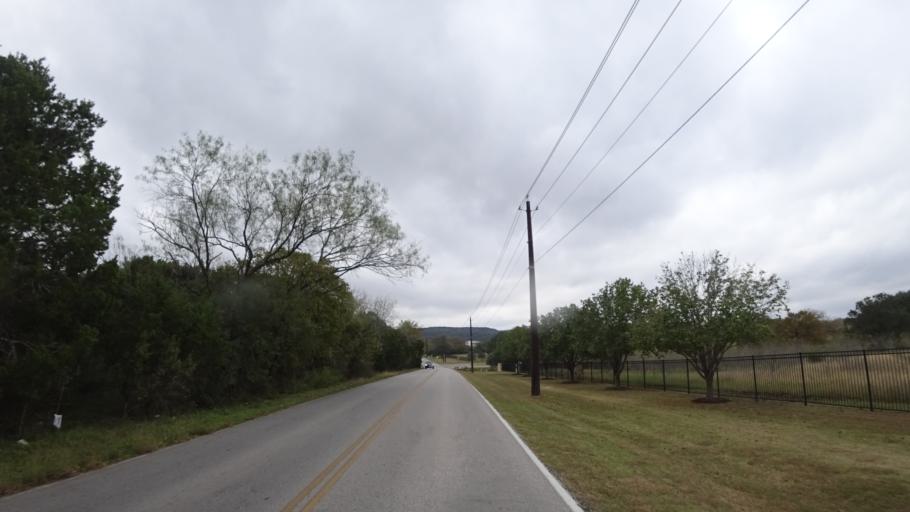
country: US
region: Texas
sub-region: Travis County
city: Bee Cave
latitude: 30.3354
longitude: -97.9219
